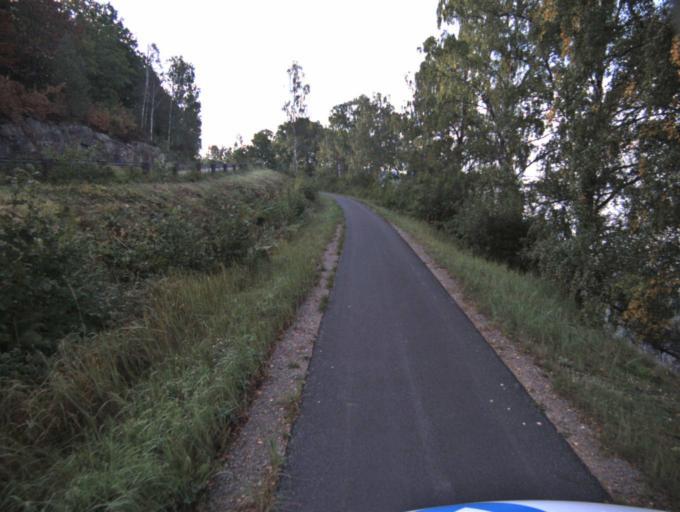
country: SE
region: Vaestra Goetaland
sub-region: Ulricehamns Kommun
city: Ulricehamn
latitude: 57.7446
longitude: 13.3936
